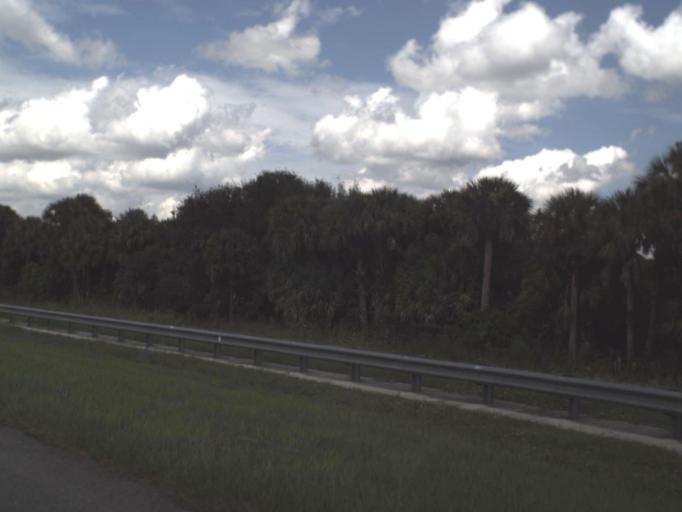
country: US
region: Florida
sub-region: Collier County
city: Immokalee
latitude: 26.3596
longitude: -81.3444
